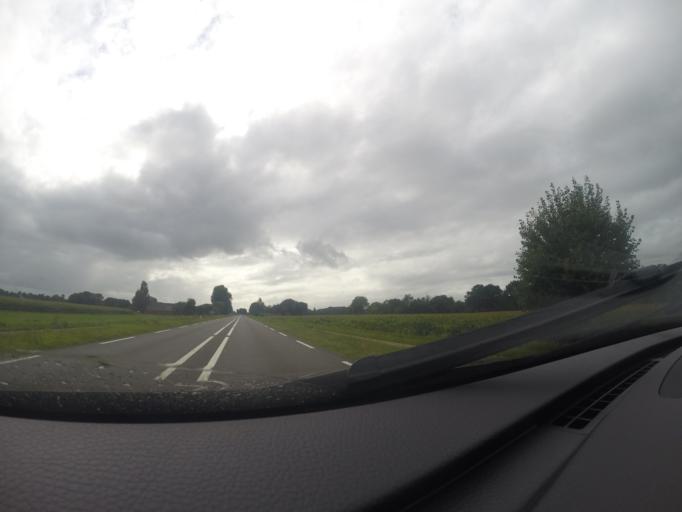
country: NL
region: Overijssel
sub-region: Gemeente Hof van Twente
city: Markelo
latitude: 52.1868
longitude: 6.4943
